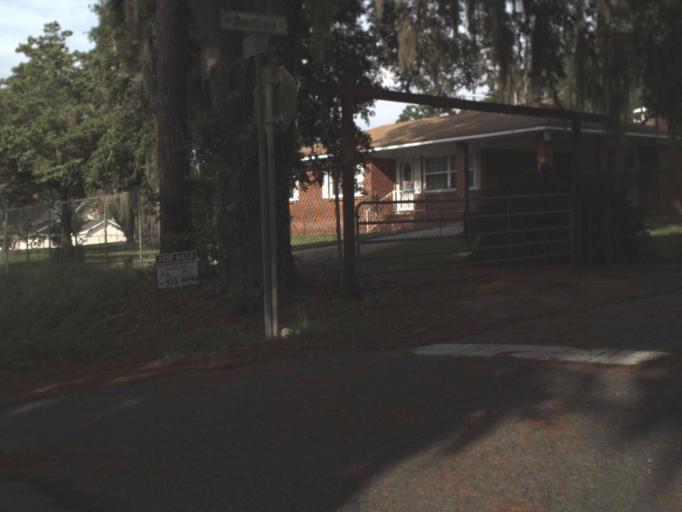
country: US
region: Florida
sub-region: Madison County
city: Madison
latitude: 30.4659
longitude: -83.6316
